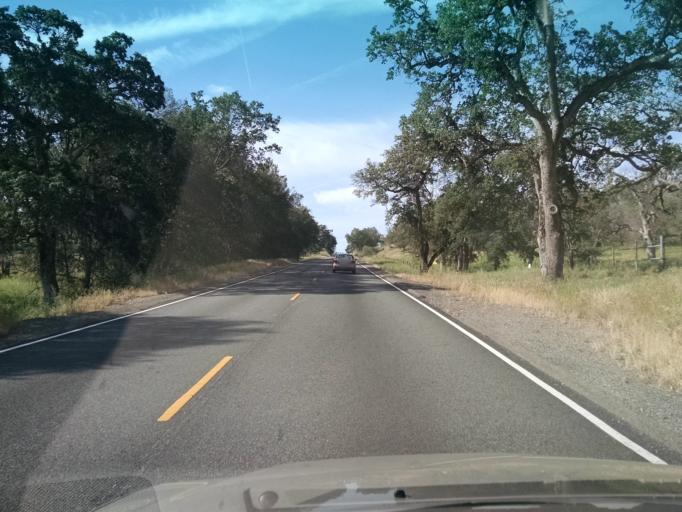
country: US
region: California
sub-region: Madera County
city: Yosemite Lakes
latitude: 37.1448
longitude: -119.7326
